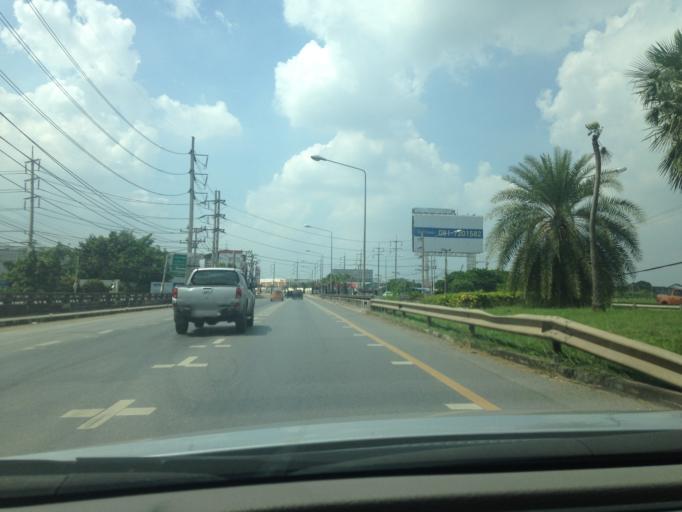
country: TH
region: Phra Nakhon Si Ayutthaya
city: Ban Bang Kadi Pathum Thani
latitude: 14.0039
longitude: 100.5660
